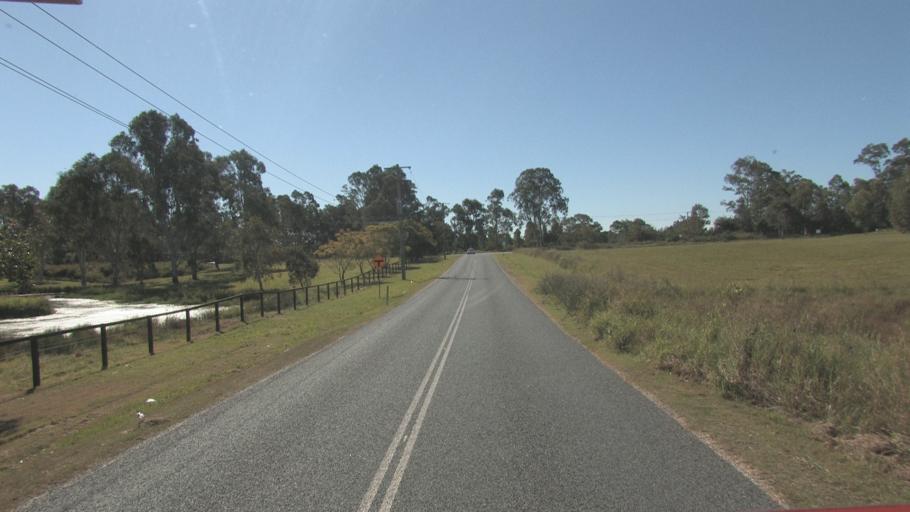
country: AU
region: Queensland
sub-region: Logan
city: Waterford West
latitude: -27.7104
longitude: 153.1408
